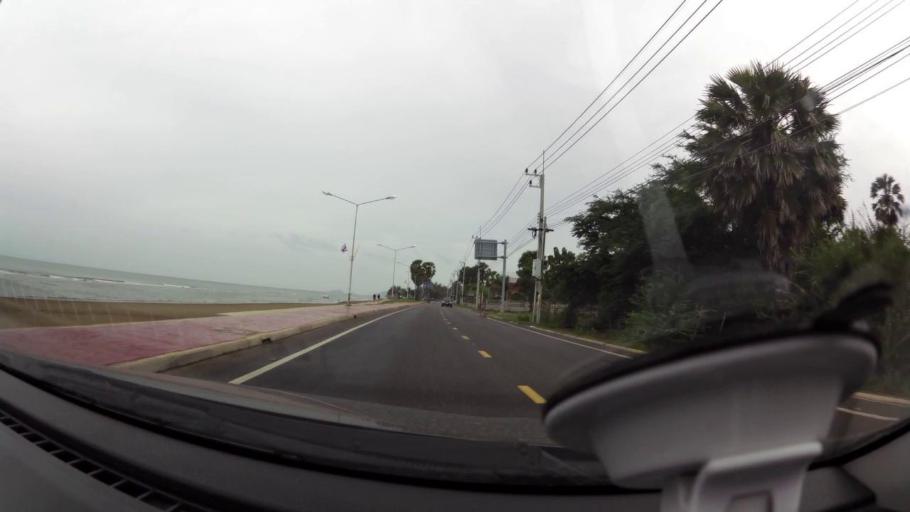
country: TH
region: Prachuap Khiri Khan
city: Pran Buri
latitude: 12.3738
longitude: 100.0001
